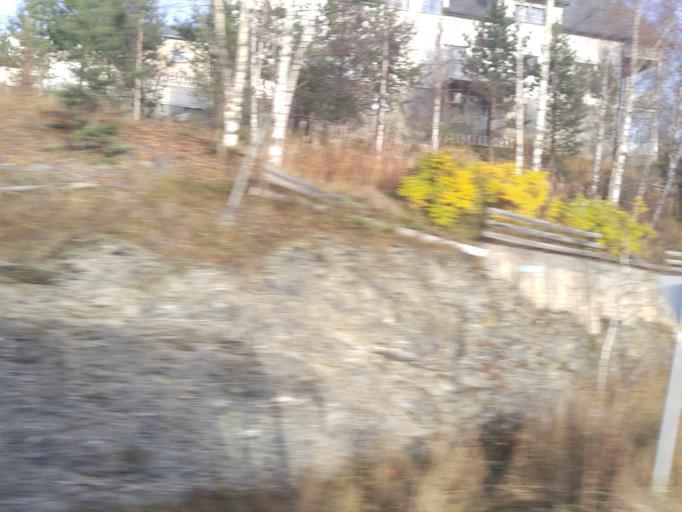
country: NO
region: Oppland
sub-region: Nord-Aurdal
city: Fagernes
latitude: 61.0641
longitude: 9.1603
